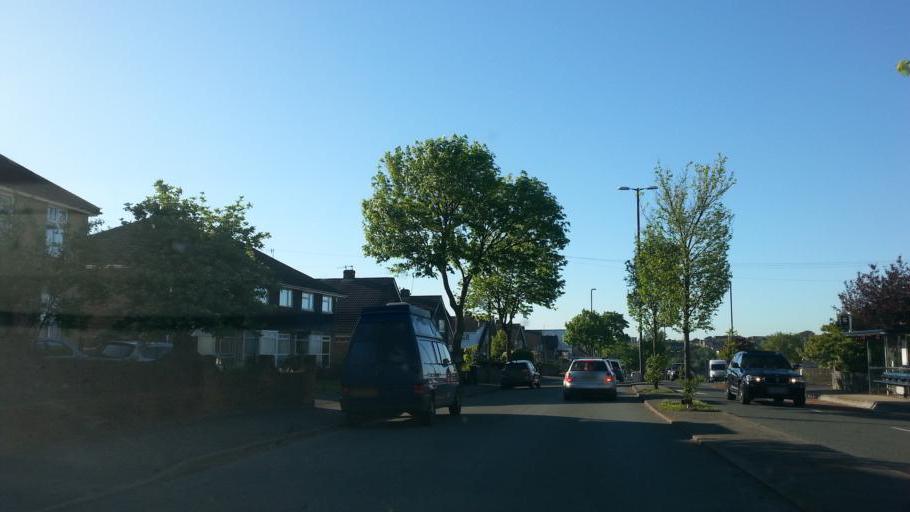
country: GB
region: England
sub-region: Bath and North East Somerset
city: Whitchurch
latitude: 51.4226
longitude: -2.5623
